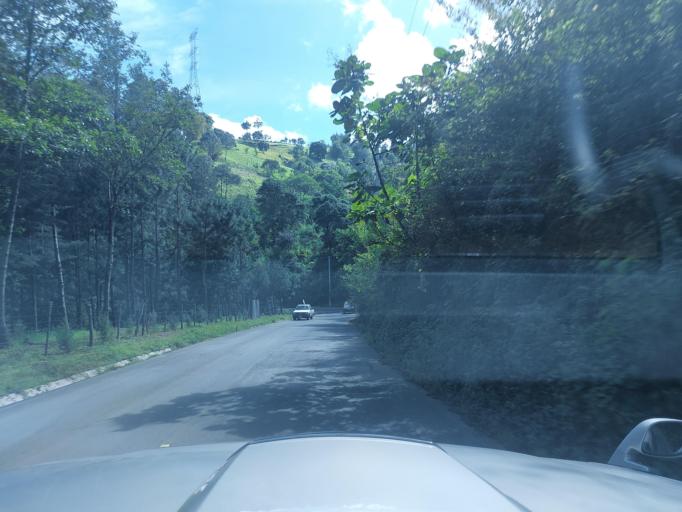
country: GT
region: Chimaltenango
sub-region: Municipio de San Juan Comalapa
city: Comalapa
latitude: 14.7139
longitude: -90.8884
